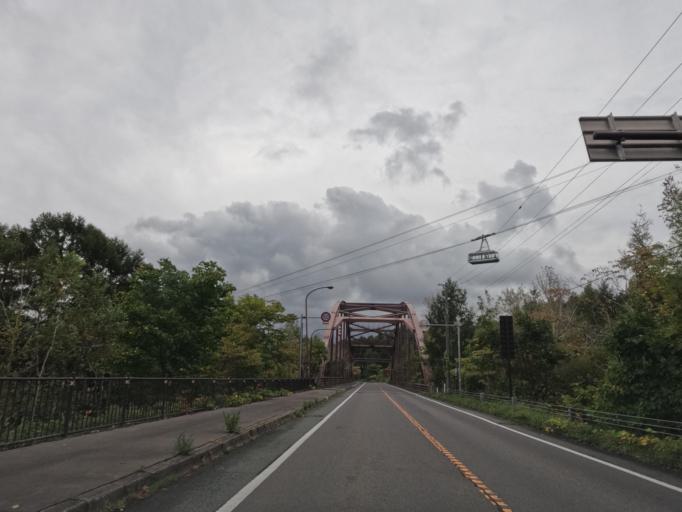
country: JP
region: Hokkaido
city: Date
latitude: 42.5402
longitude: 140.8569
